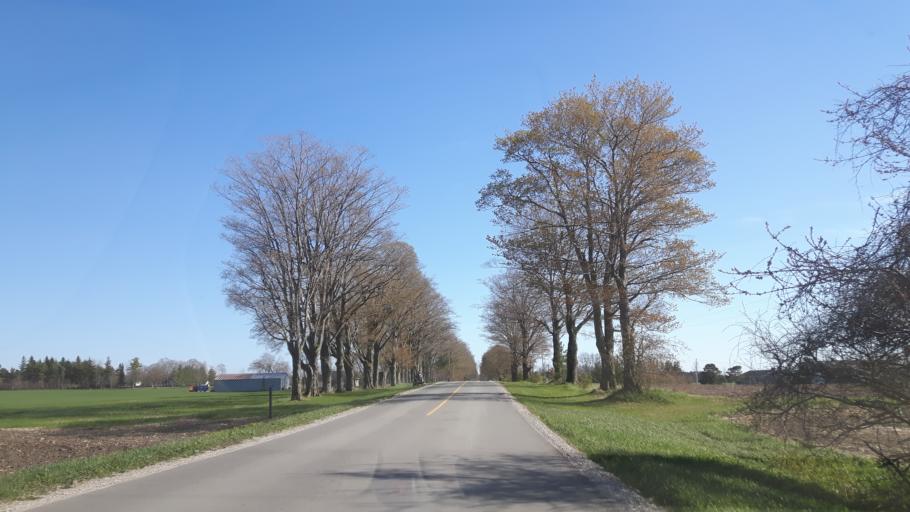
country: CA
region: Ontario
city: Goderich
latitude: 43.6283
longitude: -81.6644
